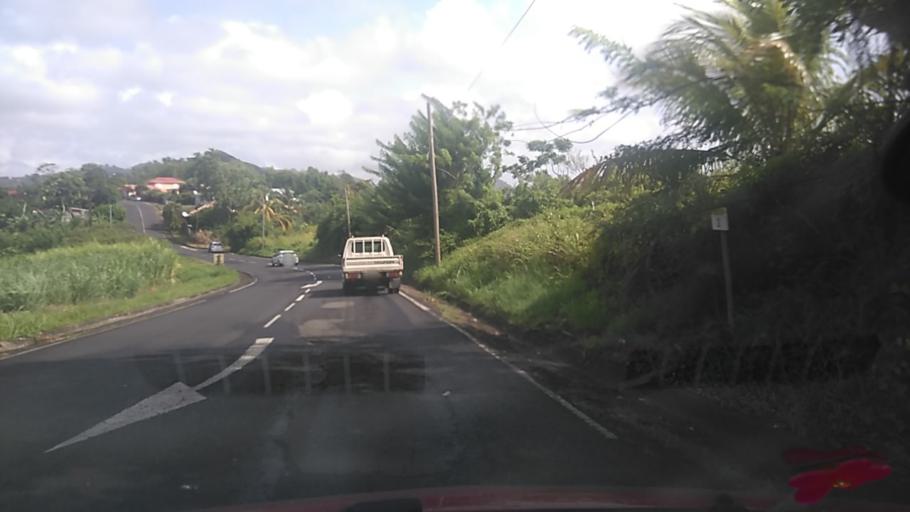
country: MQ
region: Martinique
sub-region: Martinique
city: Le Francois
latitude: 14.5924
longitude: -60.9199
